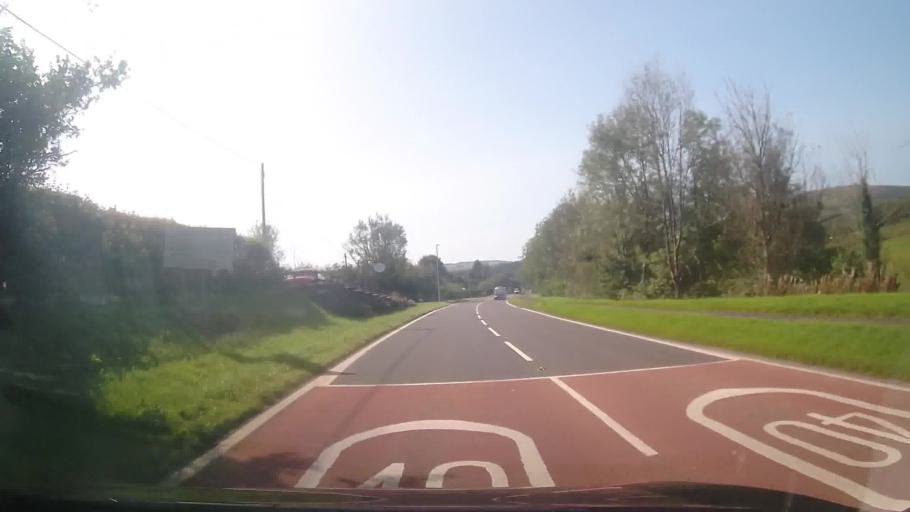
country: GB
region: Wales
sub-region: Carmarthenshire
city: Llandovery
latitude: 52.1104
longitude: -3.6338
